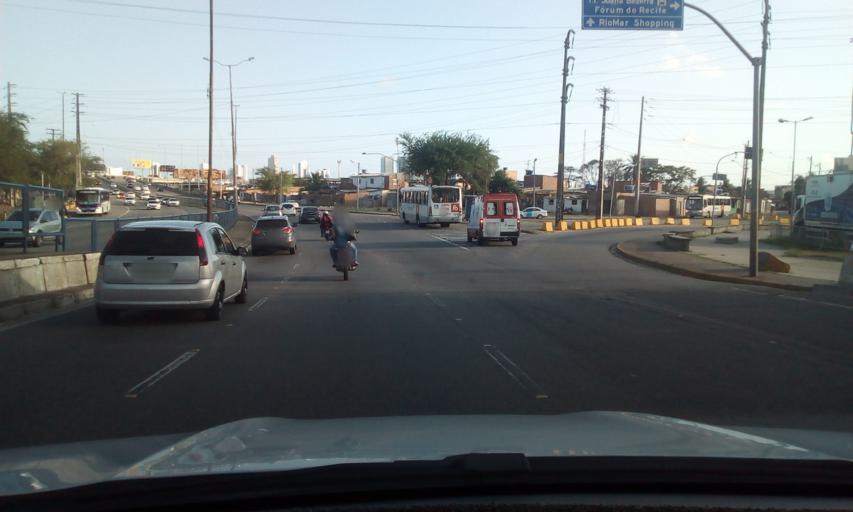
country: BR
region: Pernambuco
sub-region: Recife
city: Recife
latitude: -8.0697
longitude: -34.8966
